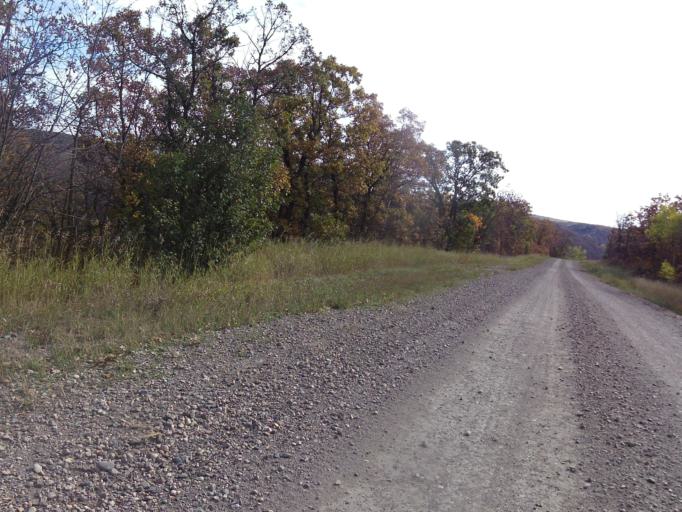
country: CA
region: Manitoba
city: Morden
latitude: 48.9489
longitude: -98.0830
